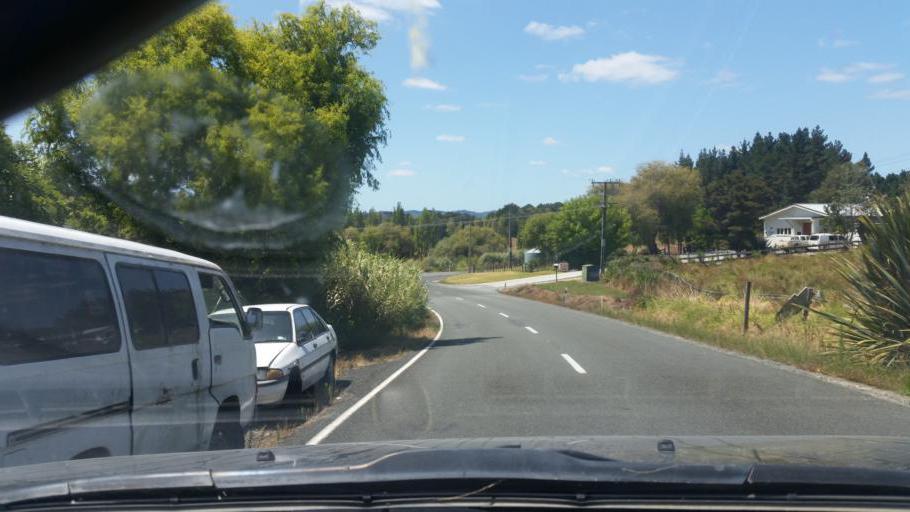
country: NZ
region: Auckland
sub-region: Auckland
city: Wellsford
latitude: -36.1240
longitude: 174.3309
